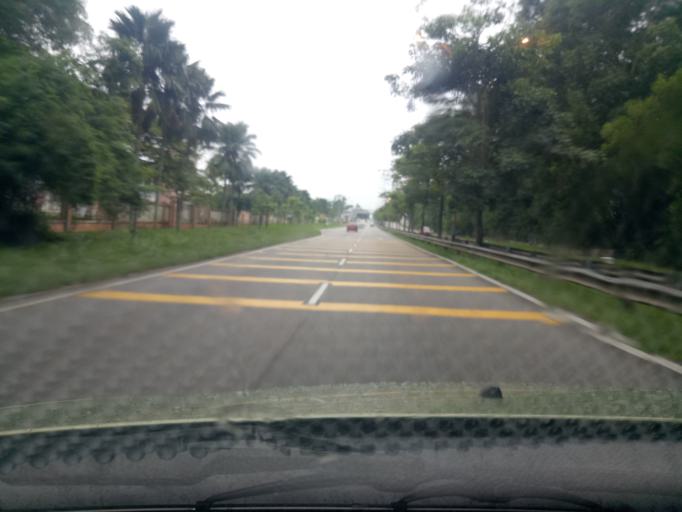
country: MY
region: Kedah
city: Sungai Petani
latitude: 5.6683
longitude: 100.5140
